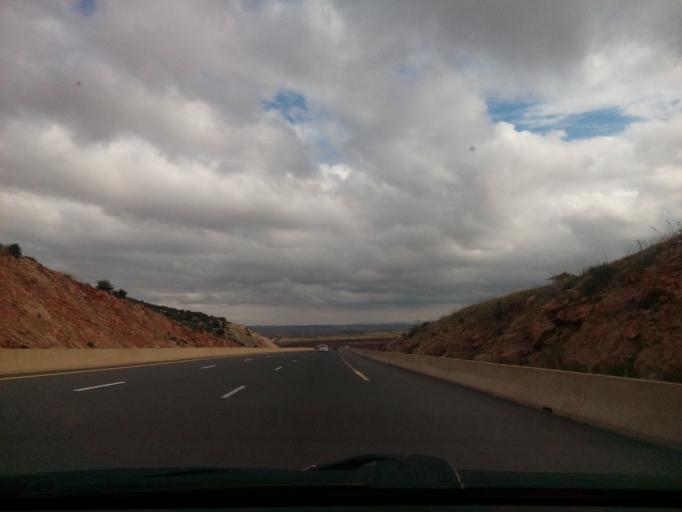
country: DZ
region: Tlemcen
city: Sidi Abdelli
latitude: 35.0198
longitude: -1.1401
